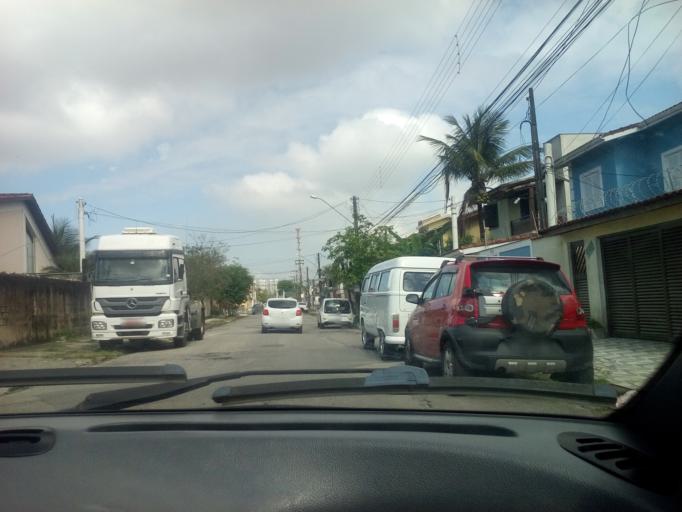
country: BR
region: Sao Paulo
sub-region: Guaruja
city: Guaruja
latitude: -23.9930
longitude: -46.2764
